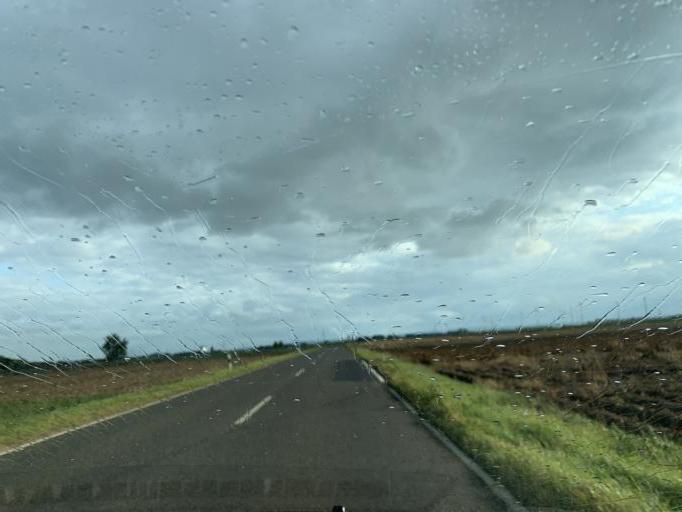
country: DE
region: North Rhine-Westphalia
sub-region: Regierungsbezirk Koln
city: Linnich
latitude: 50.9560
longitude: 6.2818
